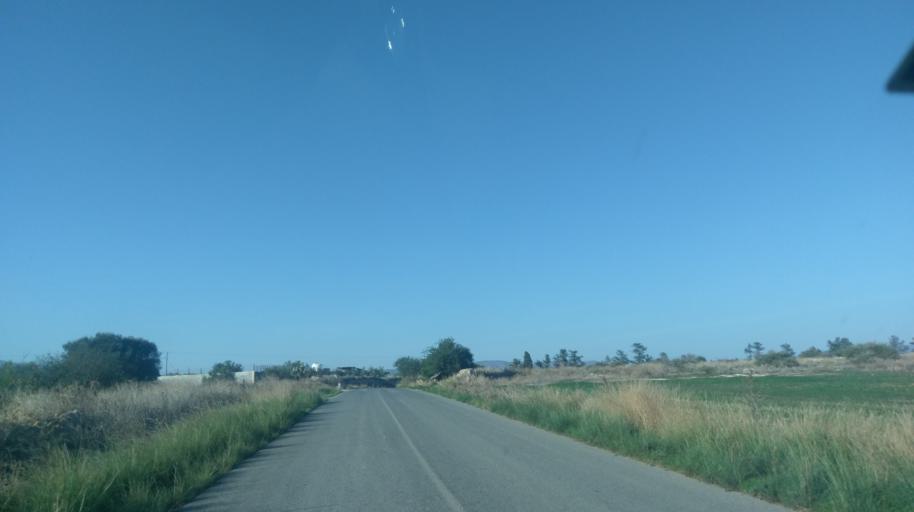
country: CY
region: Ammochostos
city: Lefkonoiko
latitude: 35.2379
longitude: 33.6825
